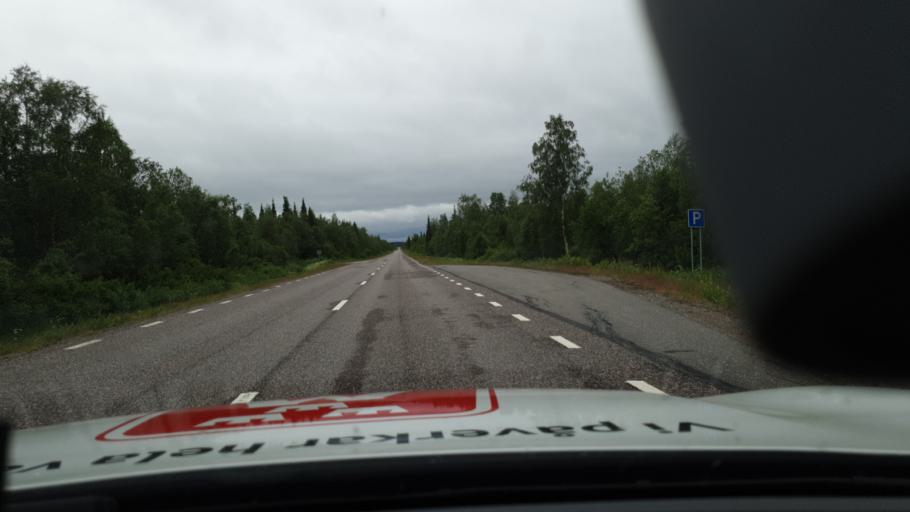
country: SE
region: Norrbotten
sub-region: Pajala Kommun
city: Pajala
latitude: 67.1274
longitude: 23.5935
